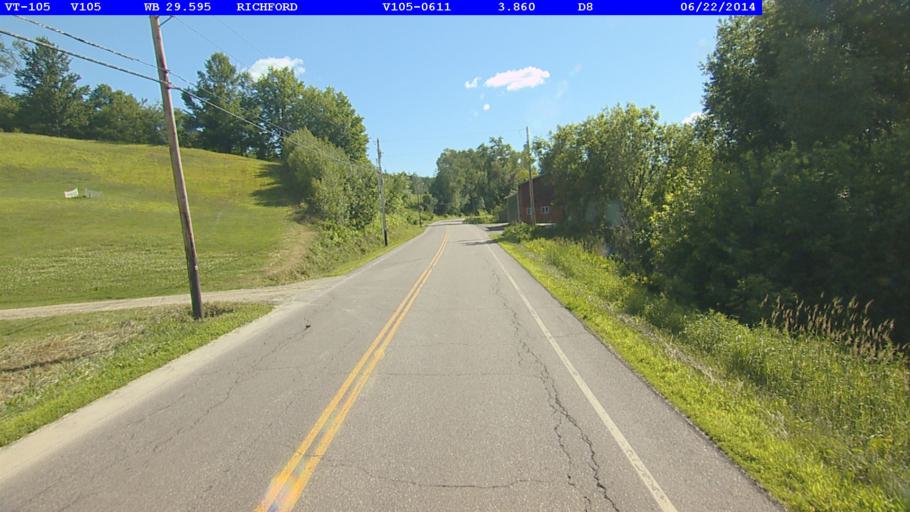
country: US
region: Vermont
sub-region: Franklin County
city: Richford
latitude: 44.9911
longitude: -72.6426
